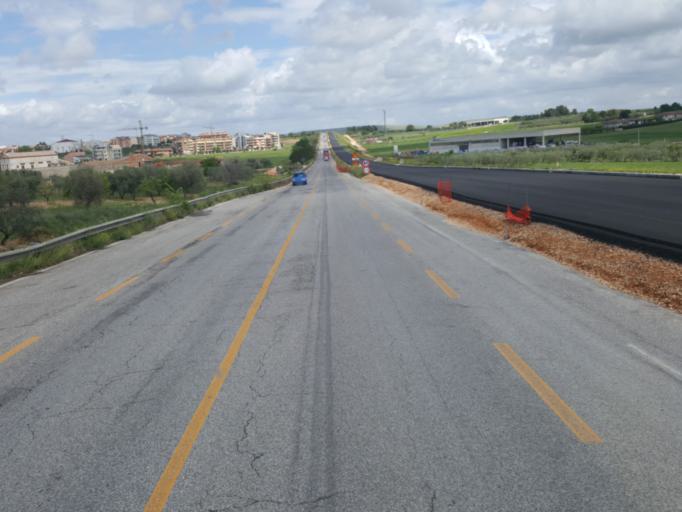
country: IT
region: Apulia
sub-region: Provincia di Bari
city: Altamura
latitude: 40.8257
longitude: 16.5708
